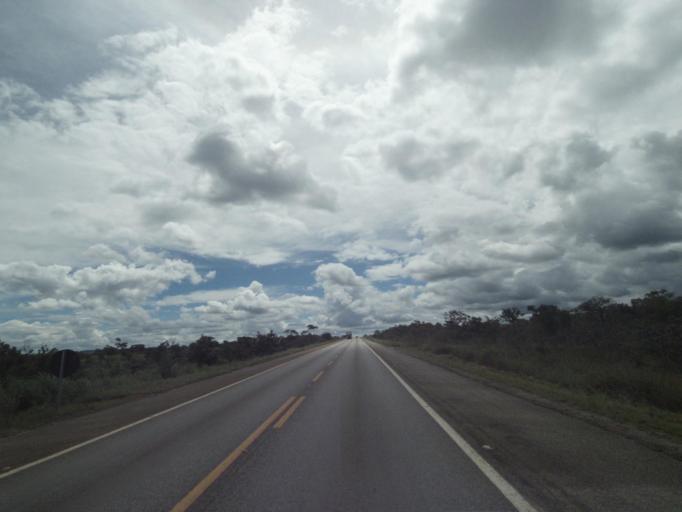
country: BR
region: Goias
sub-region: Pirenopolis
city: Pirenopolis
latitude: -15.7509
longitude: -48.6428
